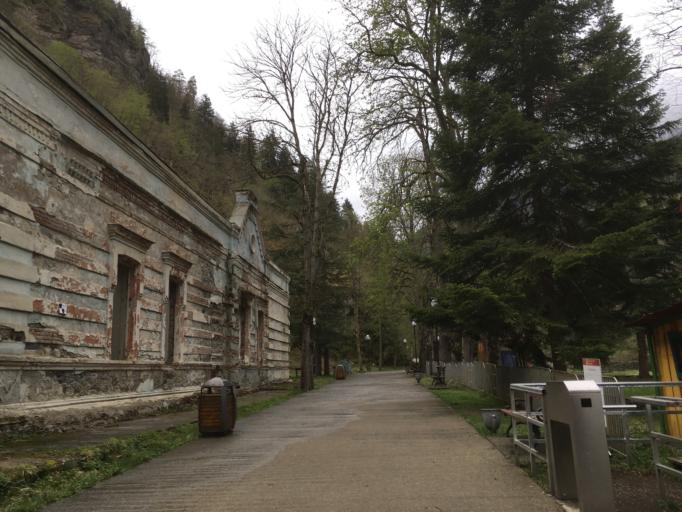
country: GE
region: Samtskhe-Javakheti
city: Borjomi
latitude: 41.8318
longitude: 43.3939
